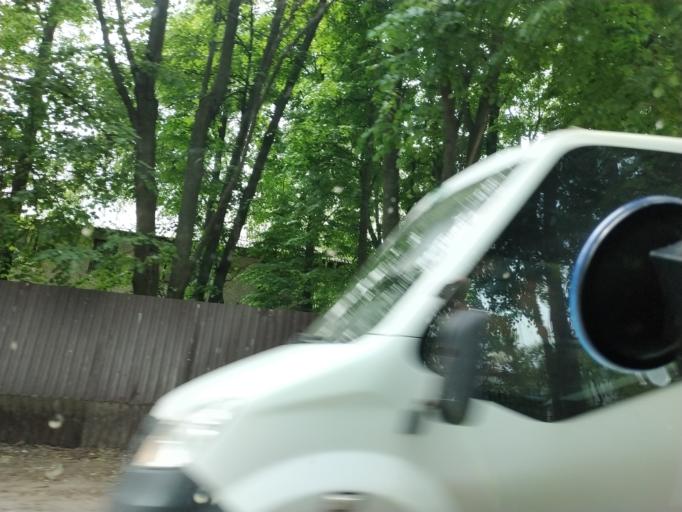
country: RU
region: Moskovskaya
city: Zhukovskiy
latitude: 55.5545
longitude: 38.1198
